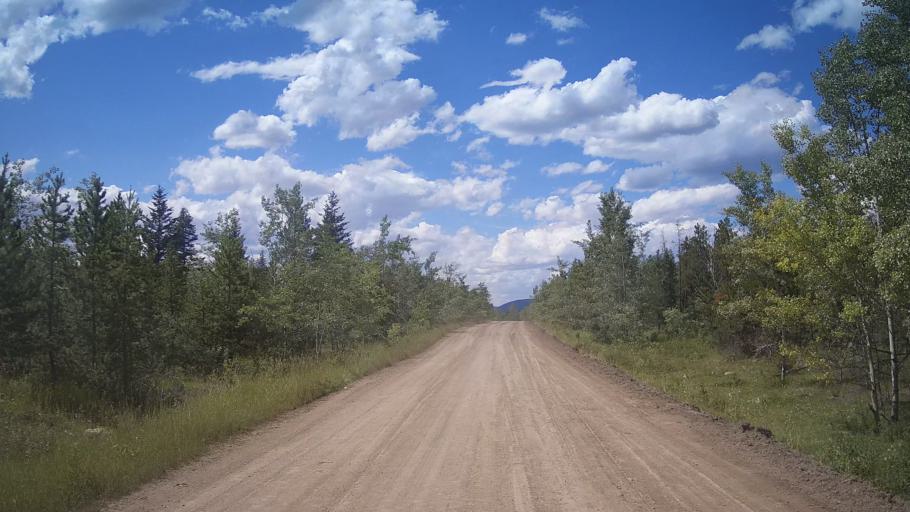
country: CA
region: British Columbia
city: Lillooet
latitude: 51.3401
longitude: -121.9202
